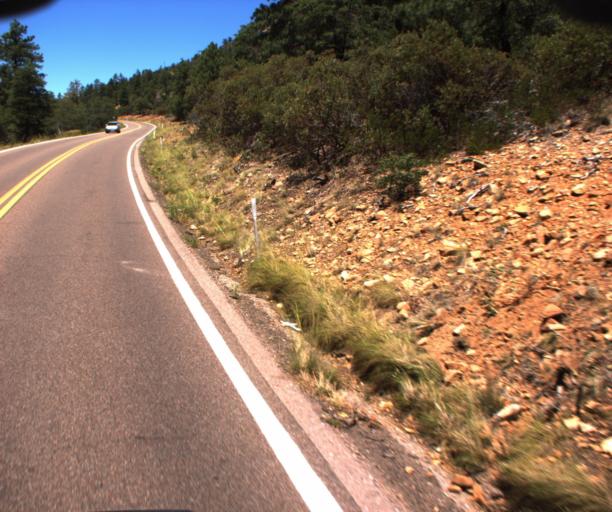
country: US
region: Arizona
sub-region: Gila County
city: Pine
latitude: 34.4013
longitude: -111.4740
